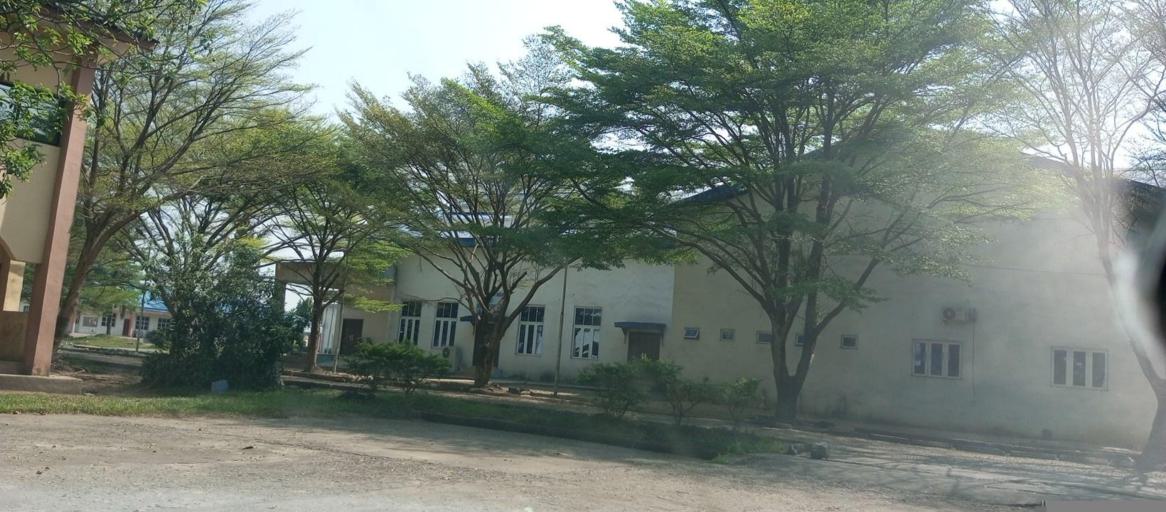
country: NG
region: Rivers
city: Emuoha
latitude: 4.9006
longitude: 6.9246
